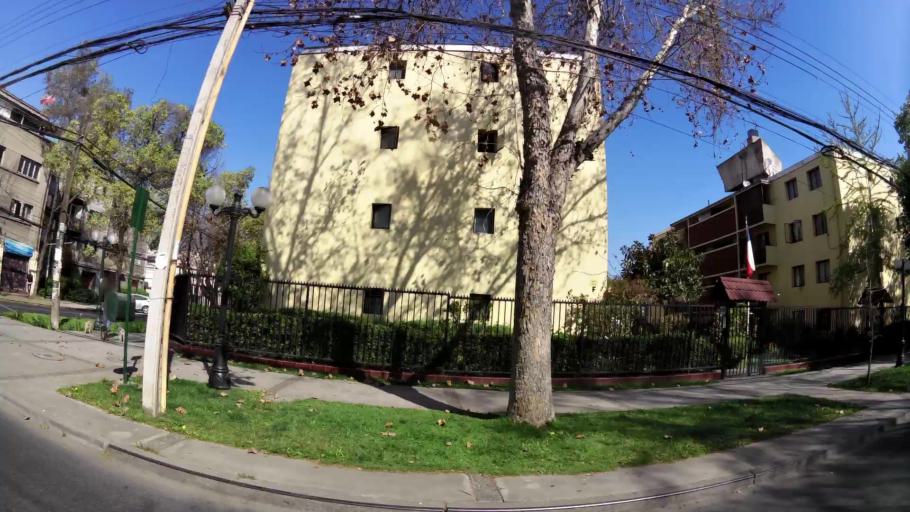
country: CL
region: Santiago Metropolitan
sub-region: Provincia de Santiago
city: Santiago
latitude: -33.4447
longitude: -70.6294
